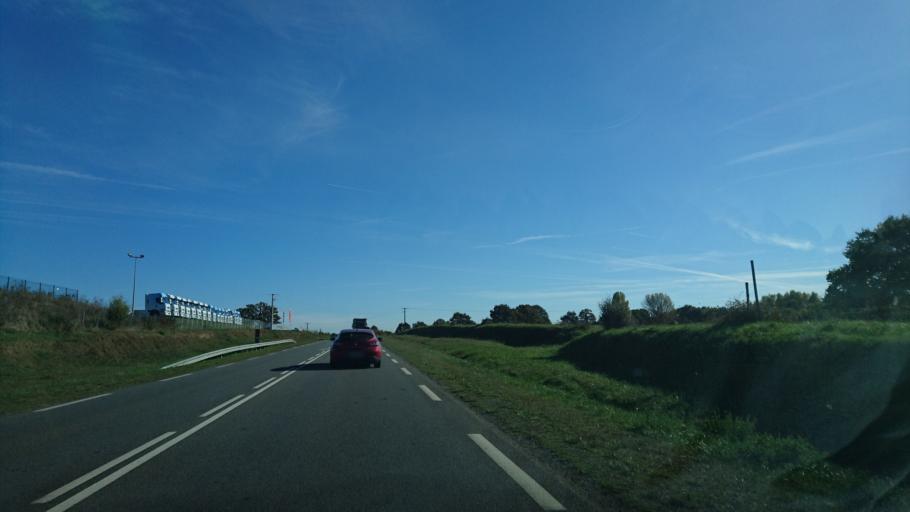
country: FR
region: Brittany
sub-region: Departement d'Ille-et-Vilaine
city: Saint-Jacques-de-la-Lande
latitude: 48.0528
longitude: -1.7234
